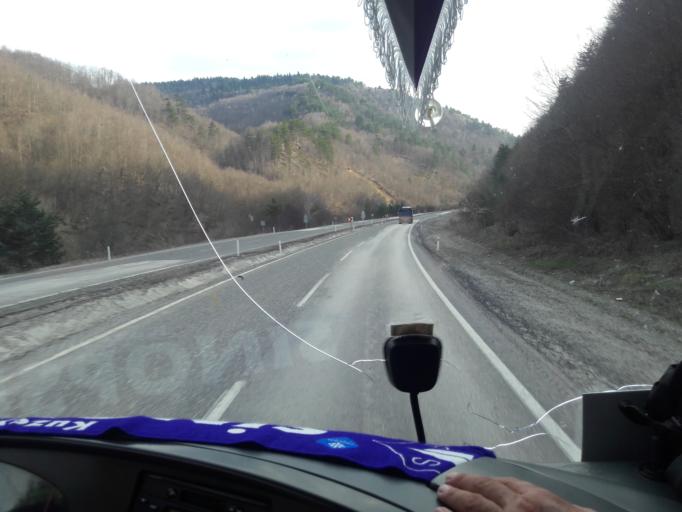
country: TR
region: Kastamonu
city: Kuzyaka
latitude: 41.1378
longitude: 33.7774
